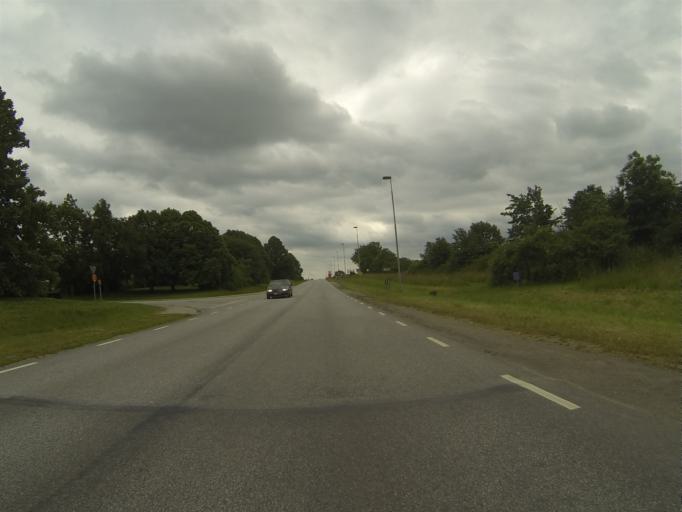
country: SE
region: Skane
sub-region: Eslovs Kommun
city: Eslov
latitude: 55.7211
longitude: 13.3314
